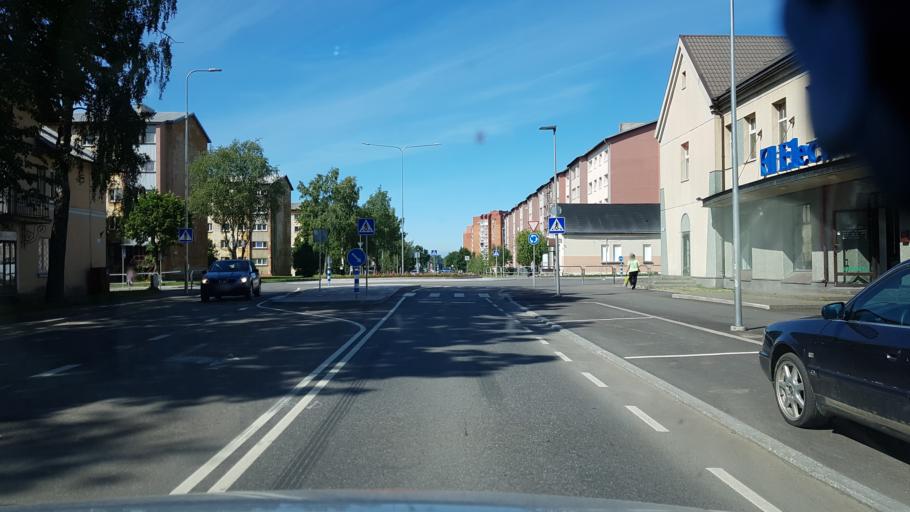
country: EE
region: Ida-Virumaa
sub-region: Kohtla-Jaerve linn
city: Kohtla-Jarve
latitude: 59.4036
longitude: 27.2858
